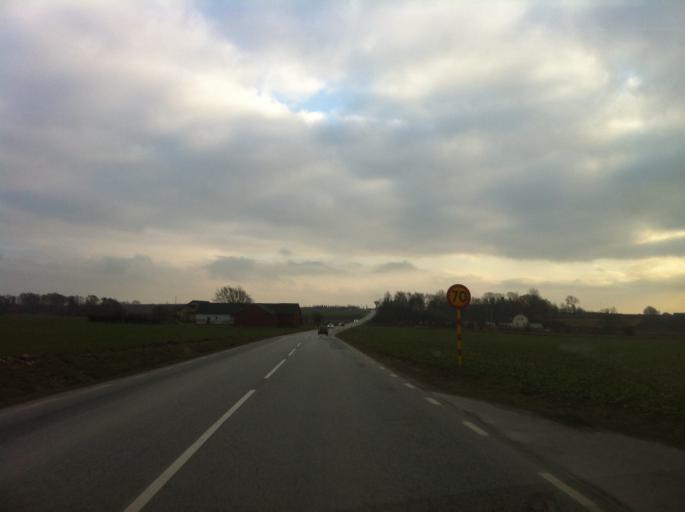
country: SE
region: Skane
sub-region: Kavlinge Kommun
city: Kaevlinge
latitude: 55.8111
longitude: 13.0919
